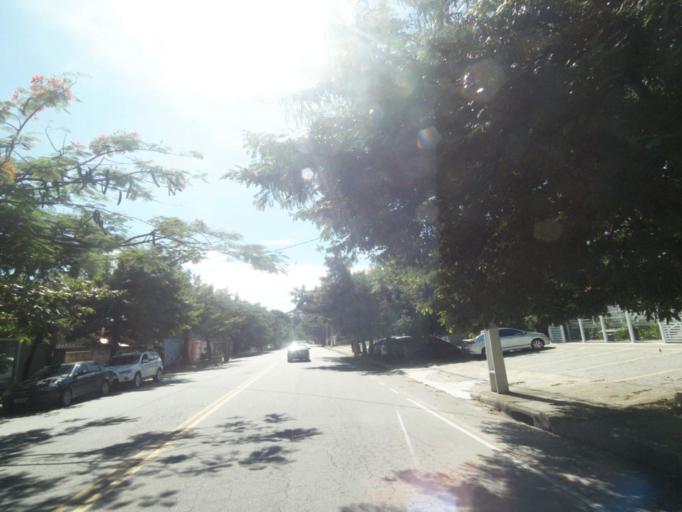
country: BR
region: Rio de Janeiro
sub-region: Niteroi
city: Niteroi
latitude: -22.9510
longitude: -43.0614
